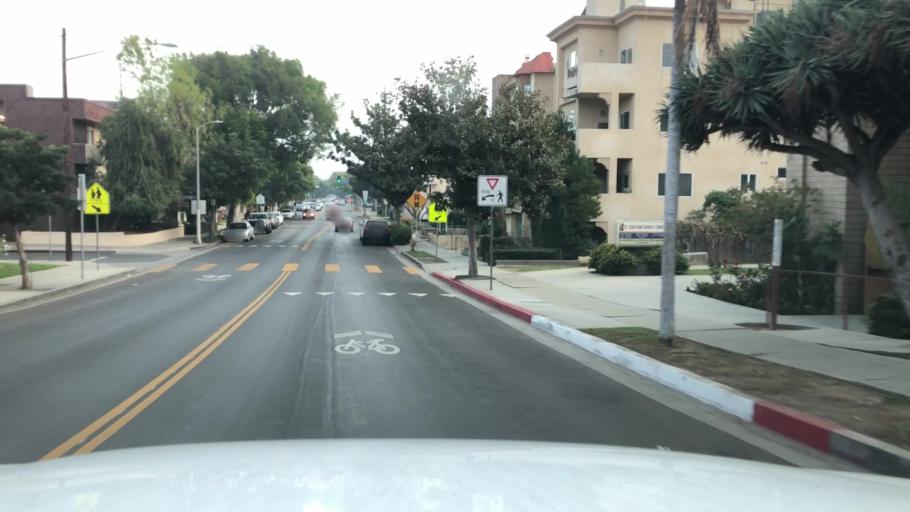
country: US
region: California
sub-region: Los Angeles County
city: Westwood, Los Angeles
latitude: 34.0468
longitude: -118.4558
